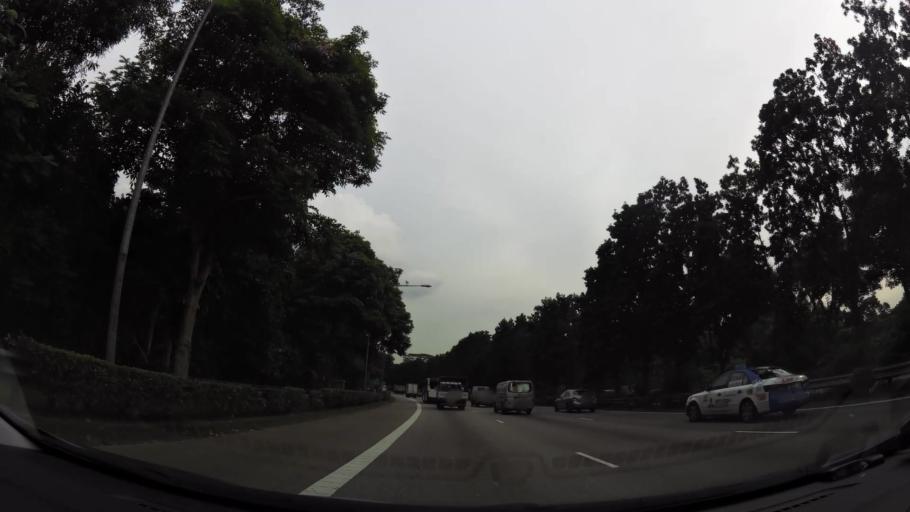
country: MY
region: Johor
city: Johor Bahru
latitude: 1.3967
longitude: 103.8147
